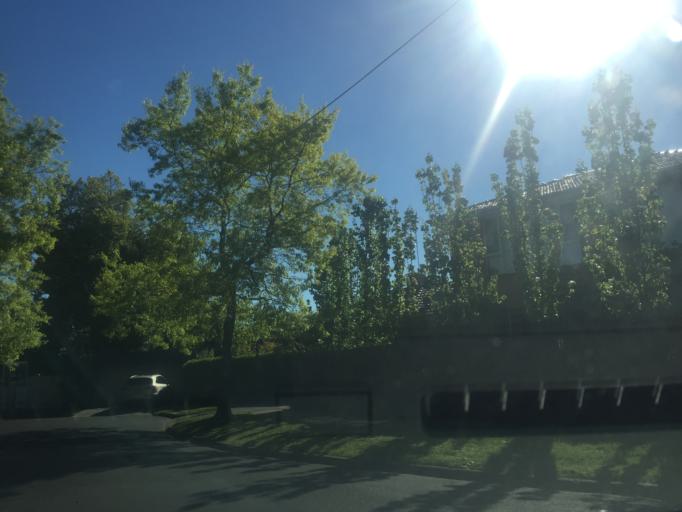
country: AU
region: Victoria
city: Balwyn
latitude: -37.8163
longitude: 145.0743
